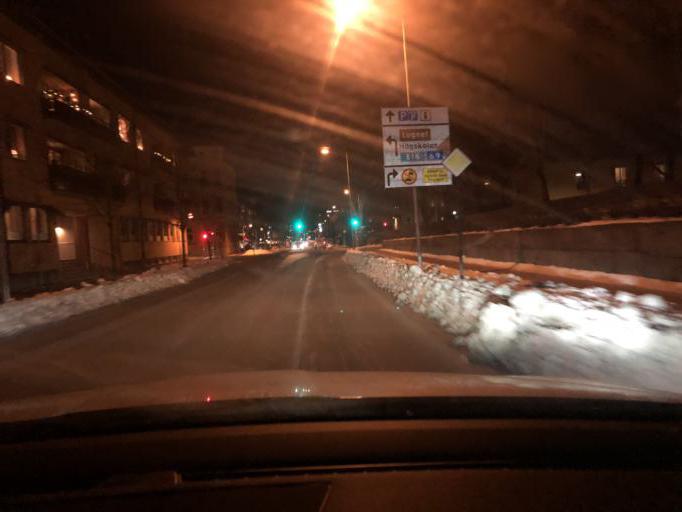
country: SE
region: Dalarna
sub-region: Faluns Kommun
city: Falun
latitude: 60.6082
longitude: 15.6323
